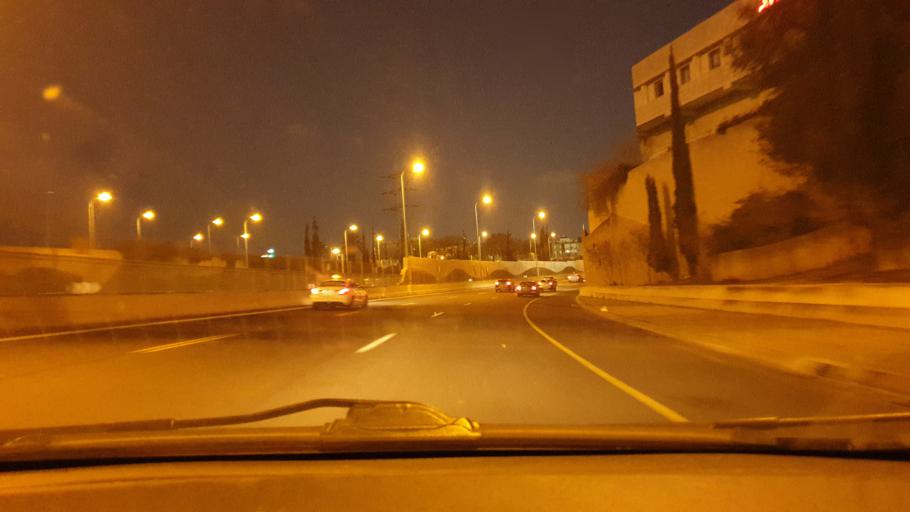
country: IL
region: Tel Aviv
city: Bat Yam
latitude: 32.0369
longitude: 34.7605
